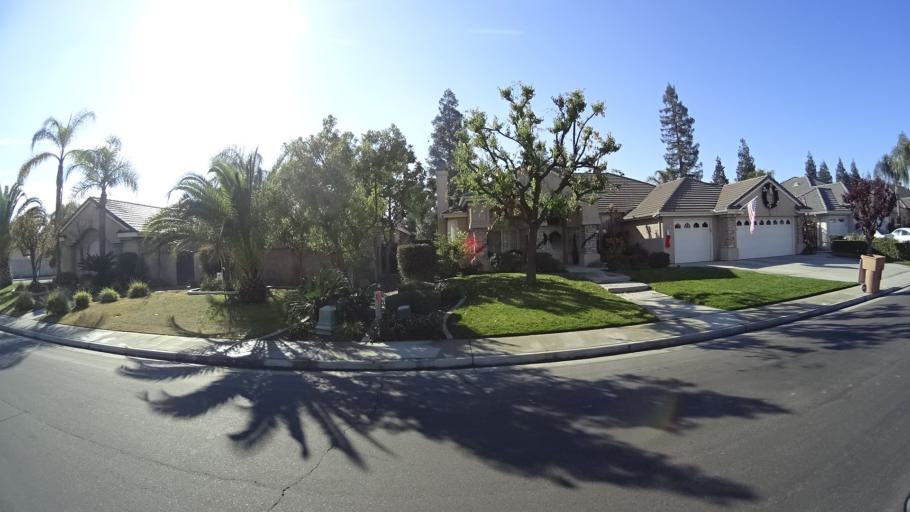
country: US
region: California
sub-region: Kern County
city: Greenacres
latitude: 35.3438
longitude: -119.1180
